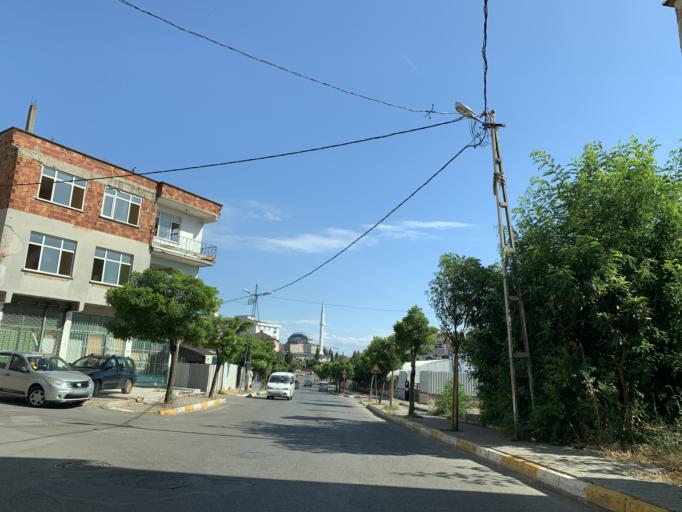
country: TR
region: Istanbul
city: Pendik
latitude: 40.8831
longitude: 29.2798
